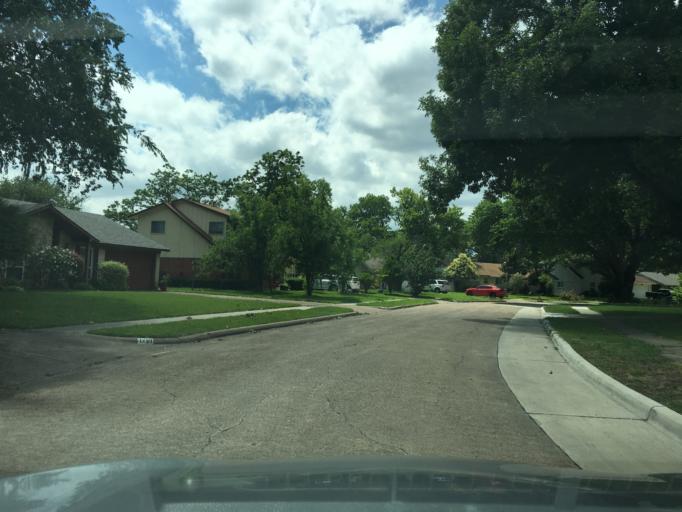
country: US
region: Texas
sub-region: Dallas County
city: Richardson
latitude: 32.9483
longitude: -96.7105
